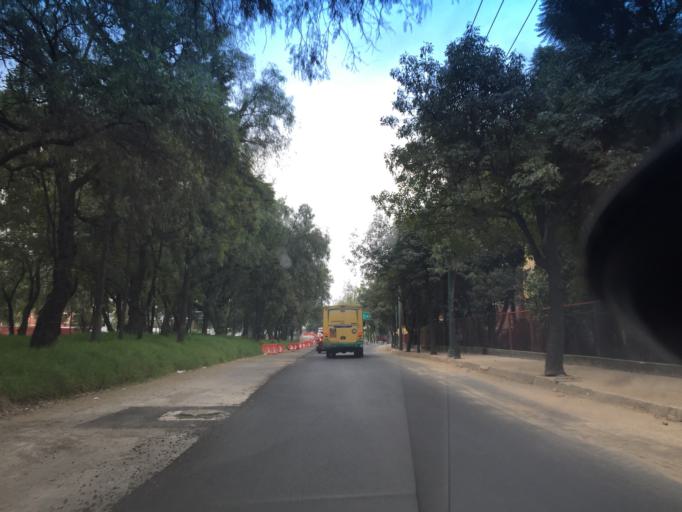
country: MX
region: Mexico
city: Vista Hermosa
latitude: 19.5112
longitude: -99.1943
